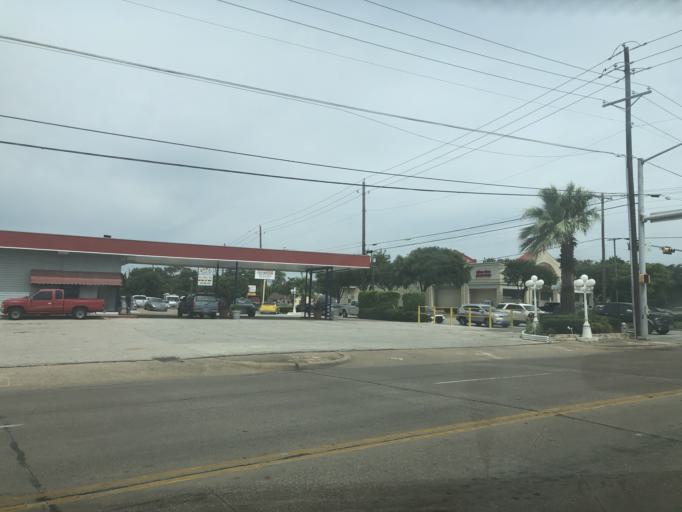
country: US
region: Texas
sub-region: Dallas County
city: Irving
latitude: 32.8000
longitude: -96.9769
